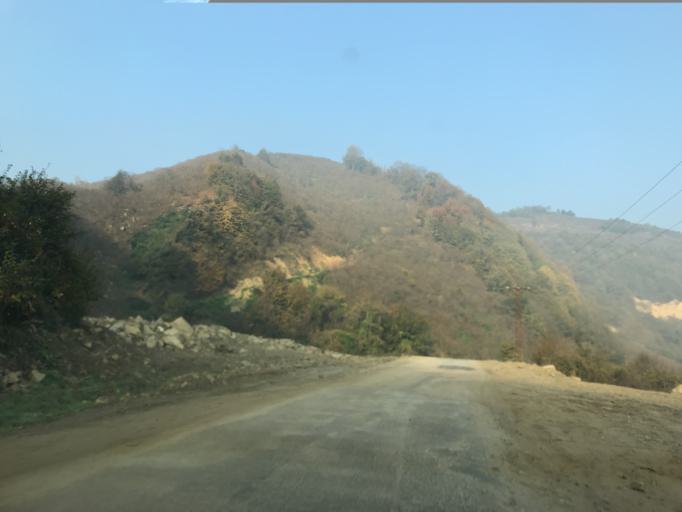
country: TR
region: Duzce
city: Cumayeri
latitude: 40.9178
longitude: 30.9310
